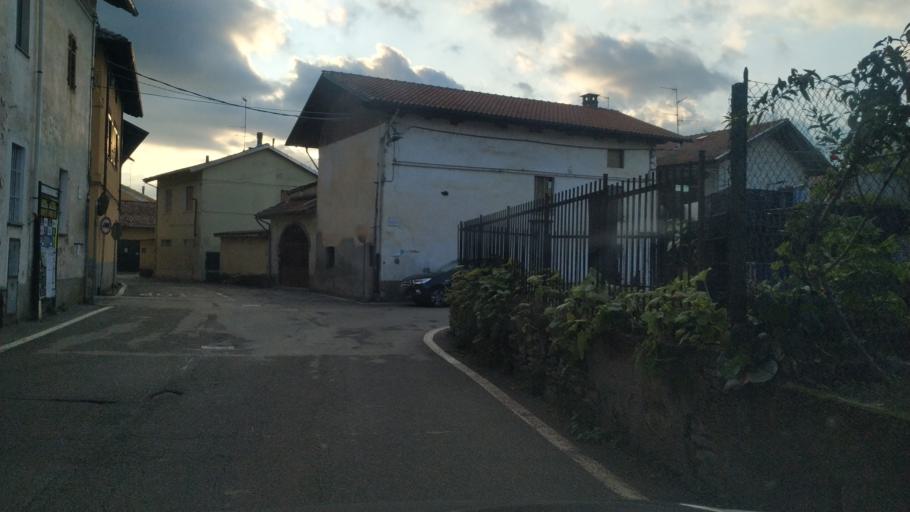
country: IT
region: Piedmont
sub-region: Provincia di Biella
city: Vergnasco
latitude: 45.4734
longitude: 8.0864
